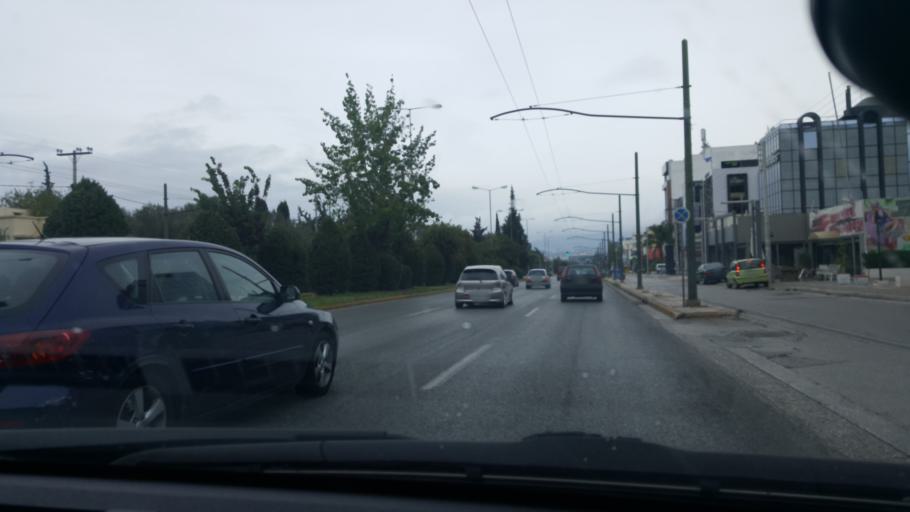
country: GR
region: Attica
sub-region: Nomarchia Athinas
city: Neo Psychiko
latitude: 38.0114
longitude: 23.7815
